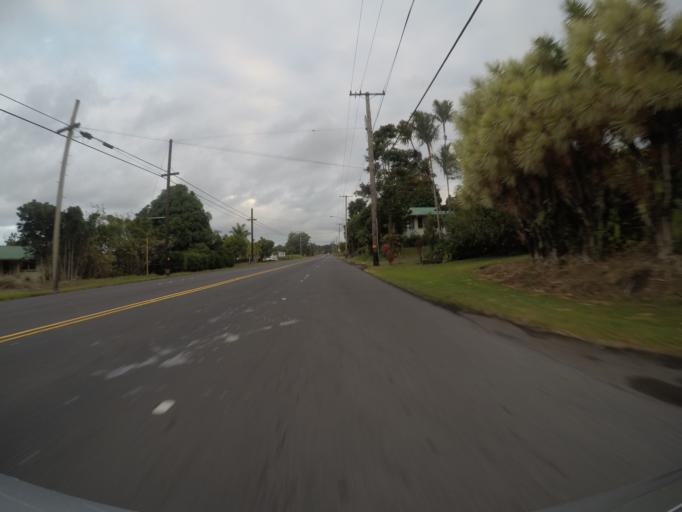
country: US
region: Hawaii
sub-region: Hawaii County
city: Hilo
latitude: 19.6797
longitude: -155.0672
